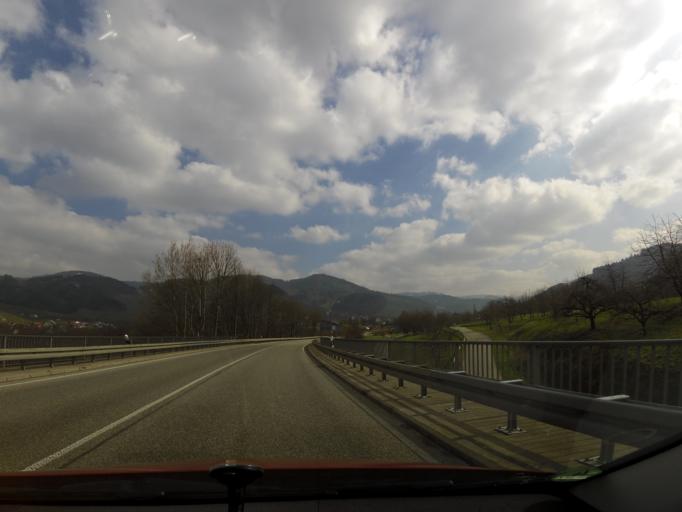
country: DE
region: Baden-Wuerttemberg
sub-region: Freiburg Region
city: Kappelrodeck
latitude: 48.5971
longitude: 8.1042
